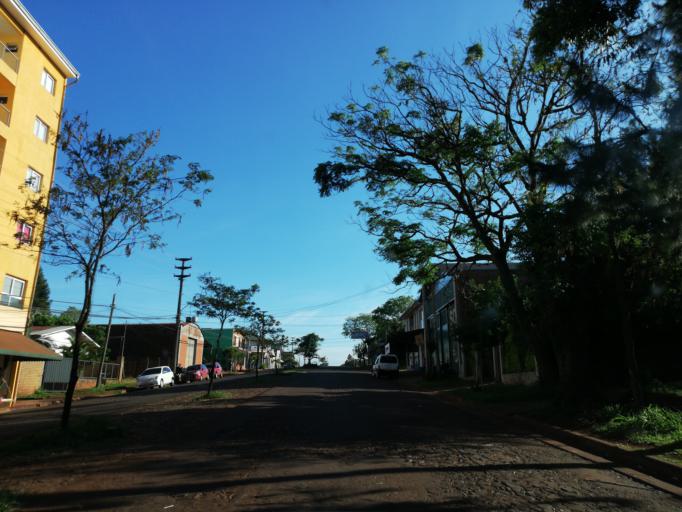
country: AR
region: Misiones
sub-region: Departamento de Obera
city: Obera
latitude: -27.5011
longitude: -55.1189
